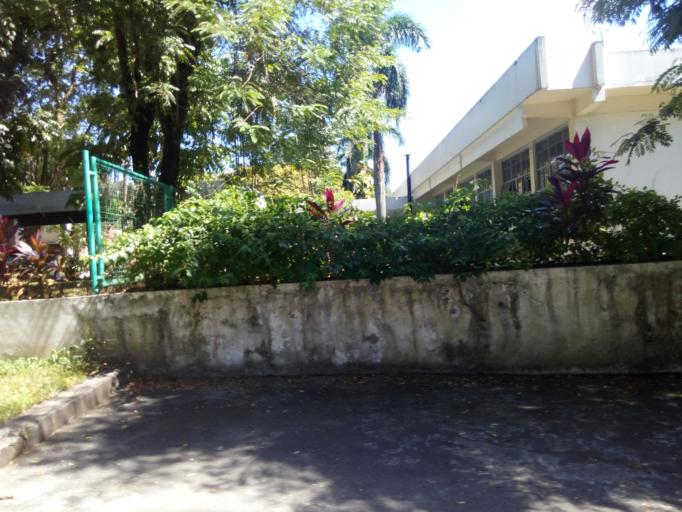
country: PH
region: Metro Manila
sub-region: Quezon City
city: Quezon City
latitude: 14.6519
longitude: 121.0688
